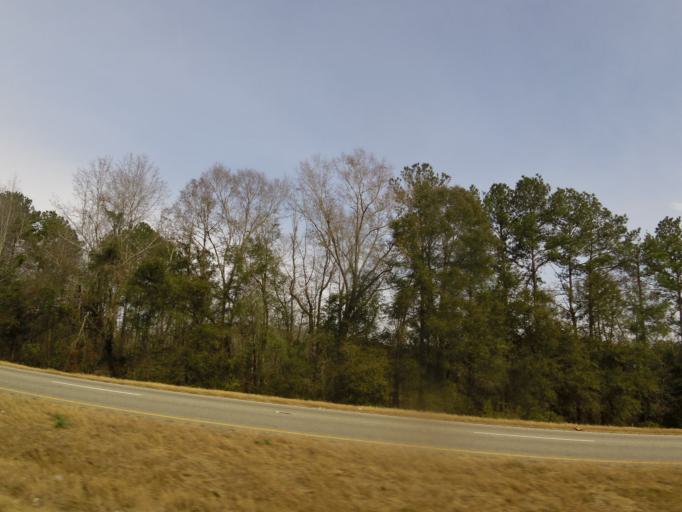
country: US
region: Alabama
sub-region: Dale County
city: Newton
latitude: 31.3859
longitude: -85.5781
